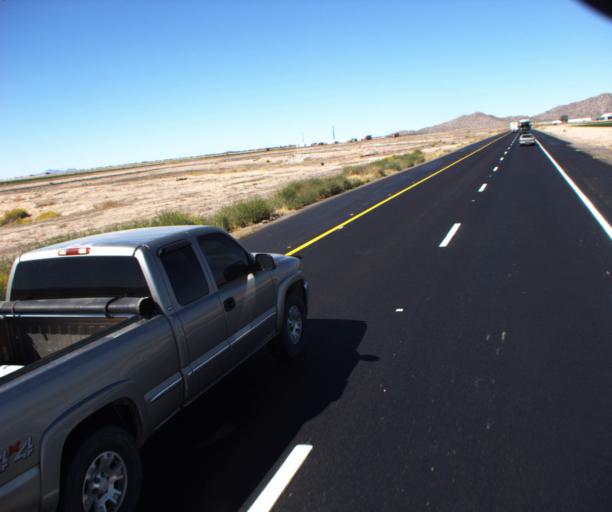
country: US
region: Arizona
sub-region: Maricopa County
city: Buckeye
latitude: 33.3984
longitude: -112.6254
